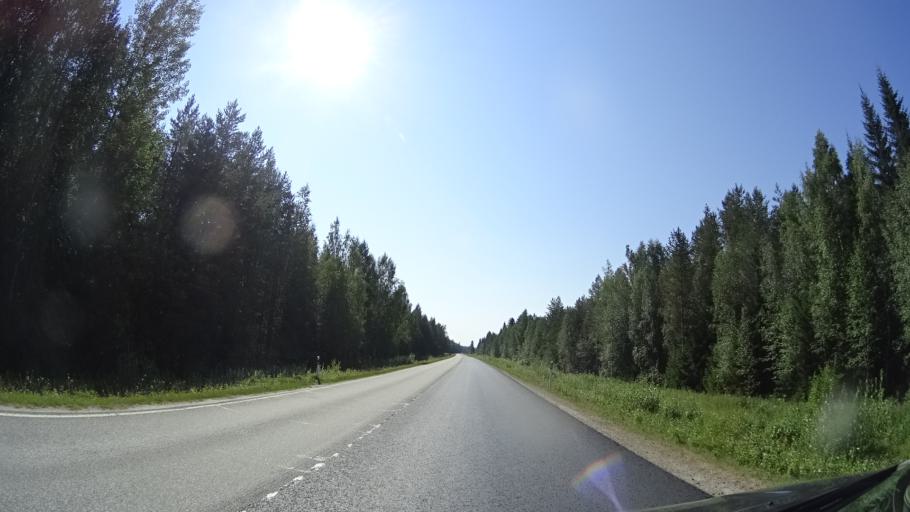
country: FI
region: North Karelia
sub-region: Joensuu
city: Juuka
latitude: 63.2257
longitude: 29.2917
